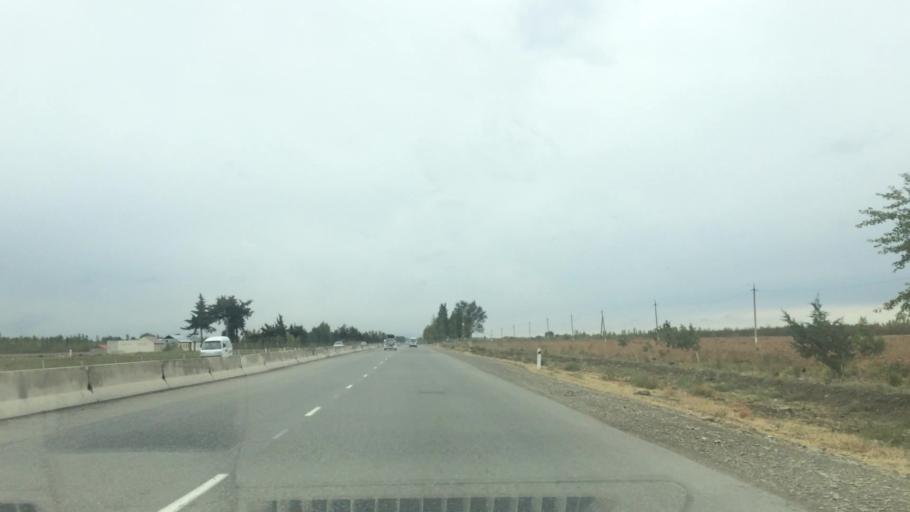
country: UZ
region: Samarqand
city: Bulung'ur
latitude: 39.7901
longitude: 67.3188
